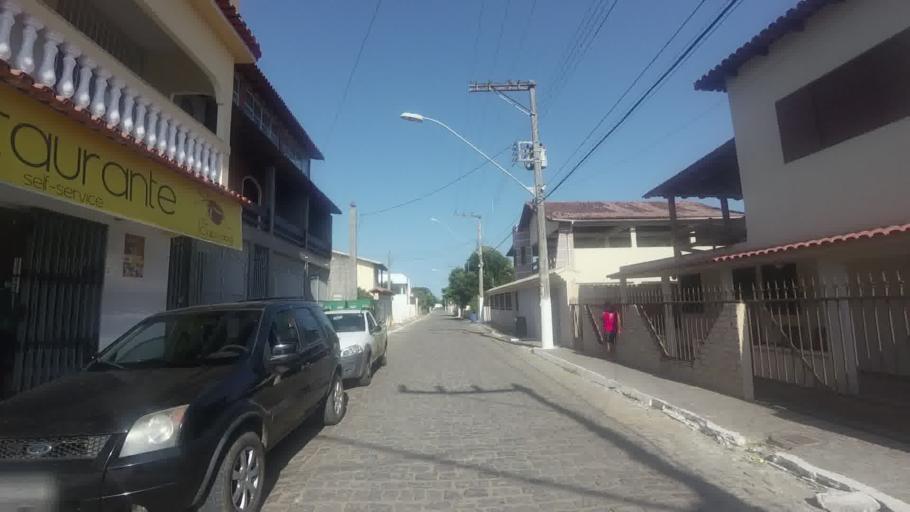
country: BR
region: Espirito Santo
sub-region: Piuma
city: Piuma
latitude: -20.8890
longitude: -40.7729
